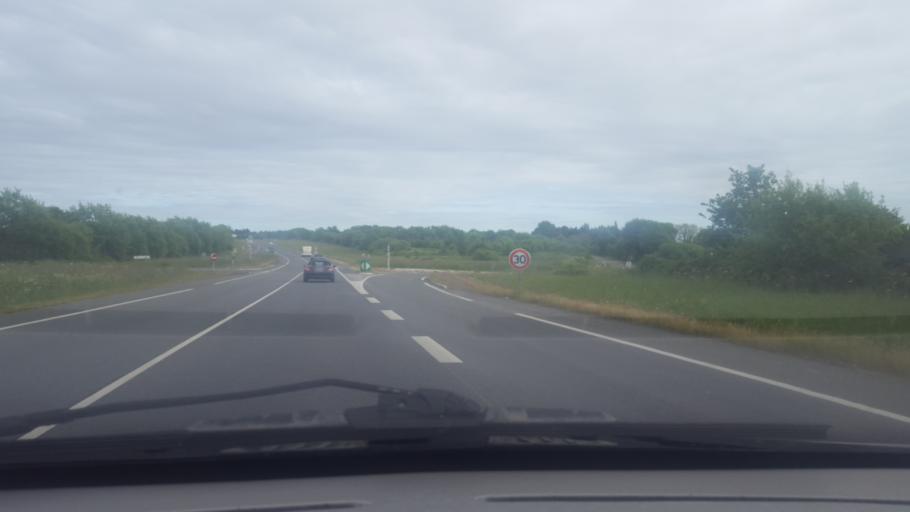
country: FR
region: Pays de la Loire
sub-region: Departement de la Loire-Atlantique
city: La Bernerie-en-Retz
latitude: 47.0805
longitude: -2.0165
